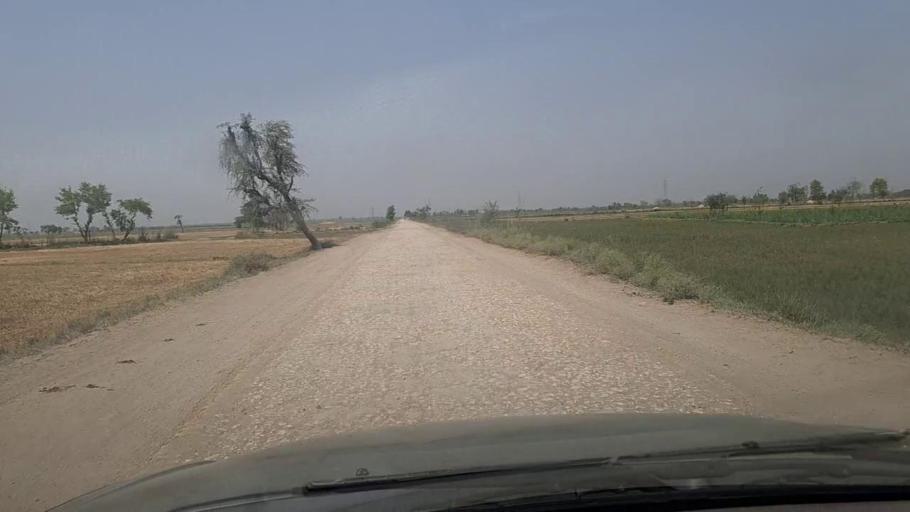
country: PK
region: Sindh
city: Adilpur
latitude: 27.9402
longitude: 69.3095
